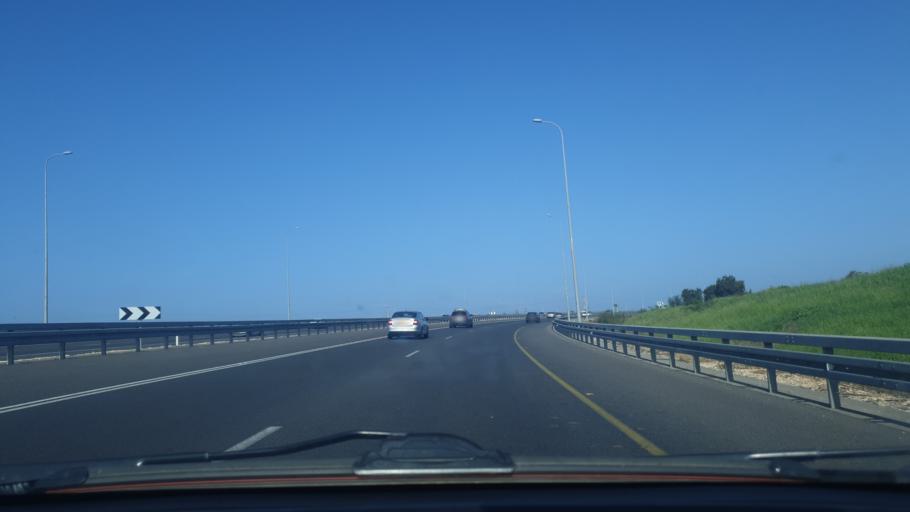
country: IL
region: Tel Aviv
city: Kefar Shemaryahu
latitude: 32.2212
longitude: 34.8328
